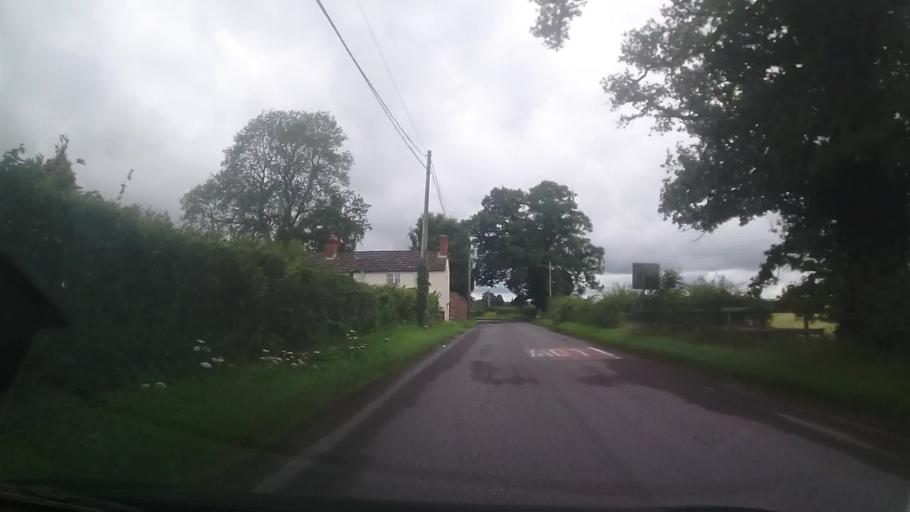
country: GB
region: England
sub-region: Shropshire
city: Petton
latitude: 52.8401
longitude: -2.8226
